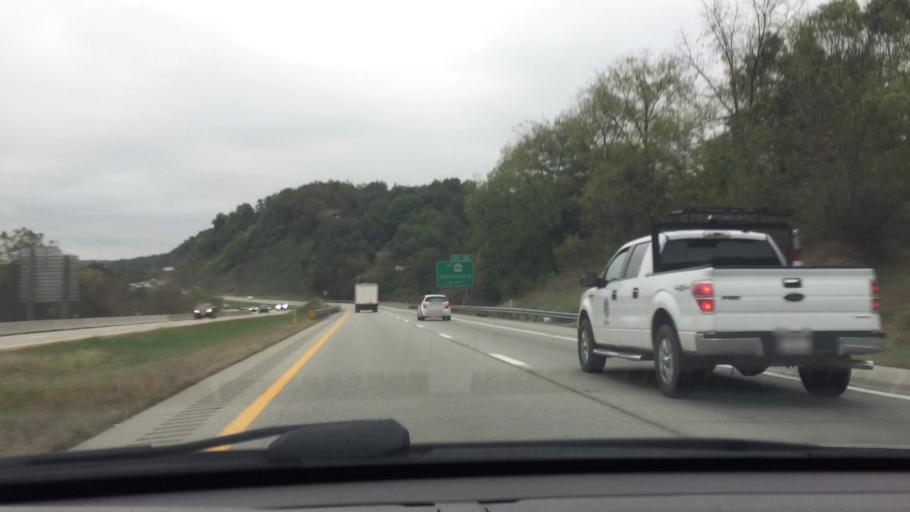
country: US
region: Pennsylvania
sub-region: Washington County
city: Canonsburg
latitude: 40.2529
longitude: -80.1863
